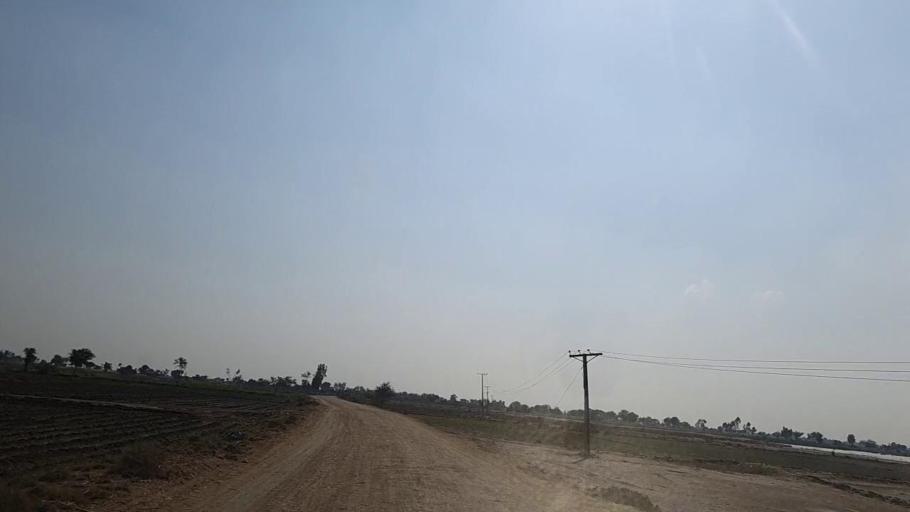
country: PK
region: Sindh
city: Daur
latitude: 26.4571
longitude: 68.2502
